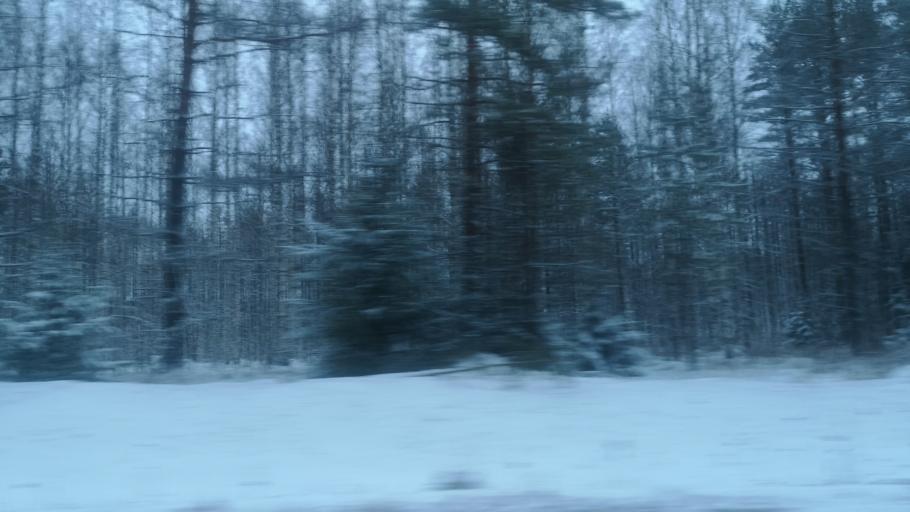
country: FI
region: Southern Savonia
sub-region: Savonlinna
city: Savonlinna
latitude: 61.9965
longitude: 28.7544
